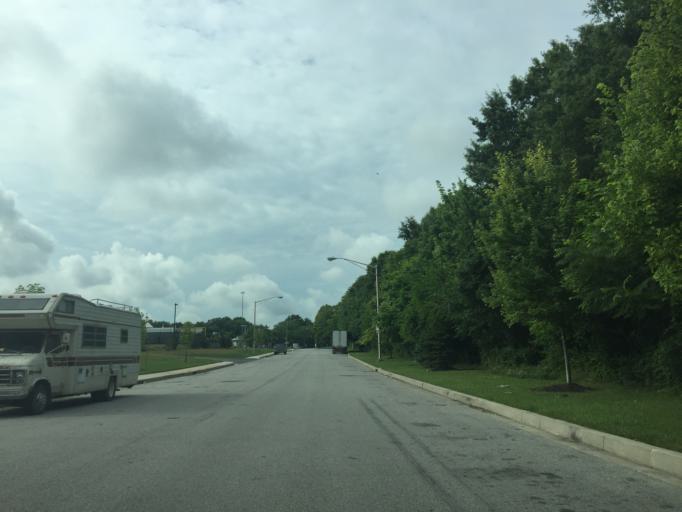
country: US
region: Maryland
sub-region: Baltimore County
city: Rosedale
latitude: 39.3122
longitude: -76.5314
